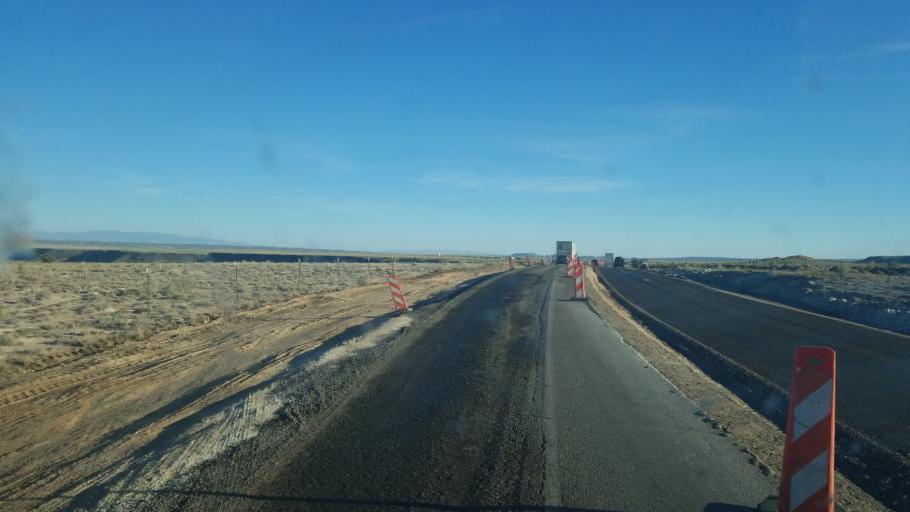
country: US
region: New Mexico
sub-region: Cibola County
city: Laguna
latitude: 34.9030
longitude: -107.0887
